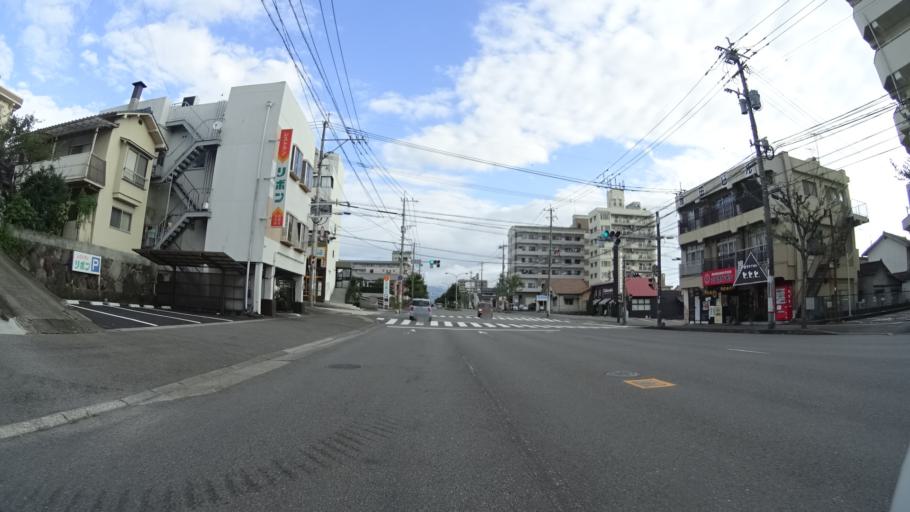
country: JP
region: Oita
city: Beppu
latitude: 33.2918
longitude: 131.4959
